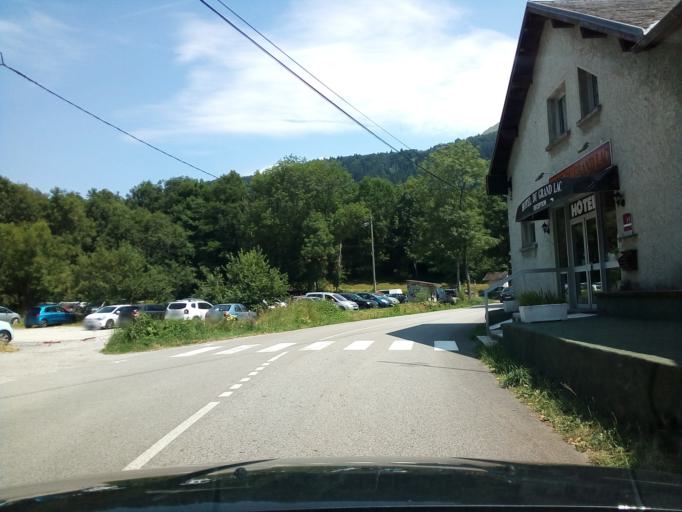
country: FR
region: Rhone-Alpes
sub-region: Departement de l'Isere
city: Notre-Dame-de-Mesage
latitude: 45.0241
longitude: 5.7817
